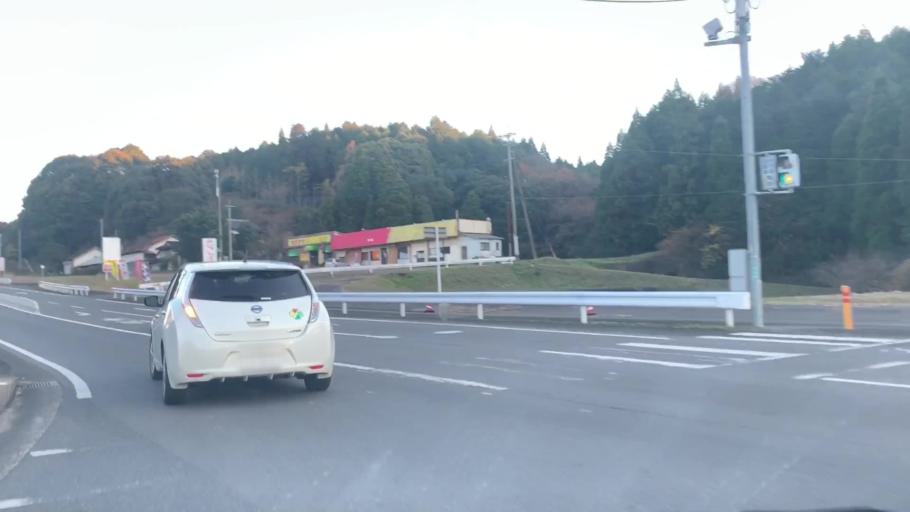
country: JP
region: Saga Prefecture
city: Imaricho-ko
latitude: 33.2637
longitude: 129.9660
